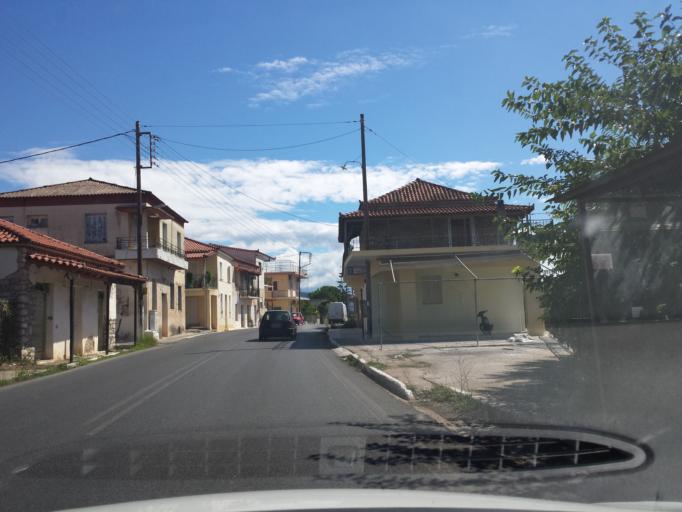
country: GR
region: Peloponnese
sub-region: Nomos Messinias
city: Messini
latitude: 37.0058
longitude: 21.9328
